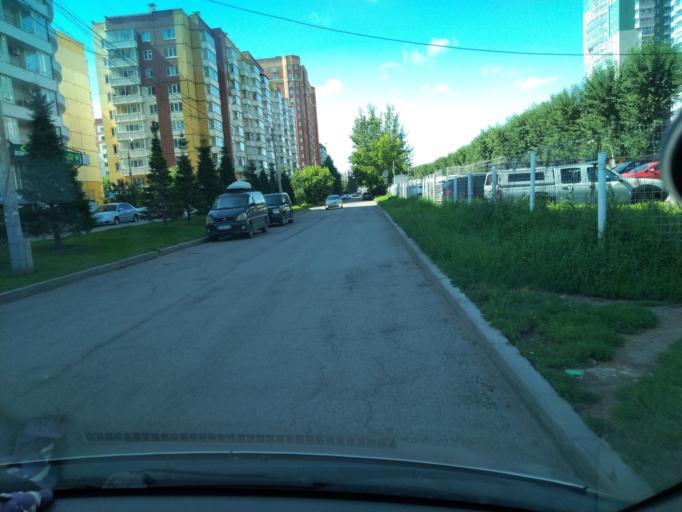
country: RU
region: Krasnoyarskiy
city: Krasnoyarsk
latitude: 56.0457
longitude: 92.9023
